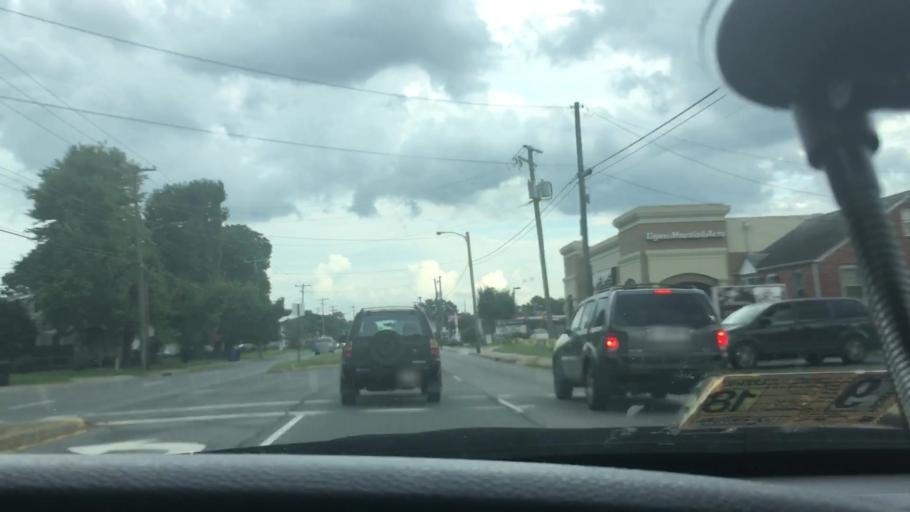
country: US
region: Virginia
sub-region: City of Portsmouth
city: Portsmouth Heights
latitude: 36.8203
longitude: -76.3843
